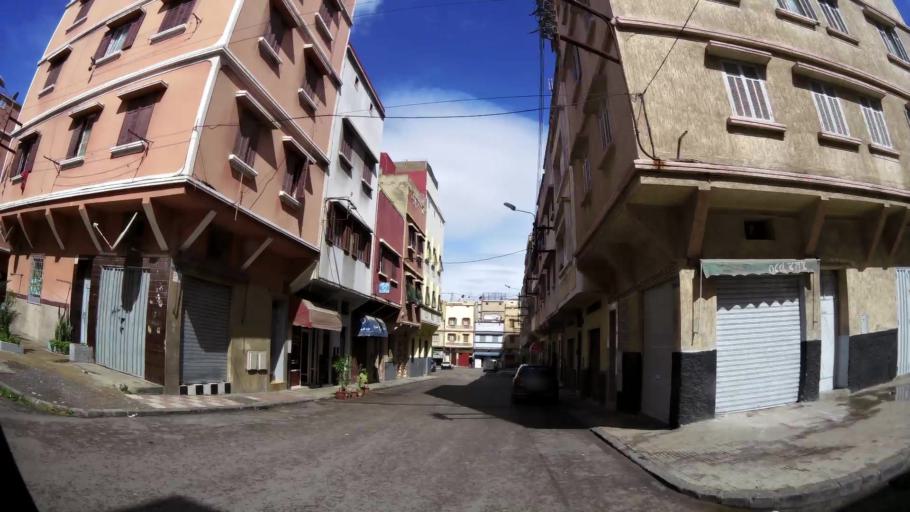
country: MA
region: Grand Casablanca
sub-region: Casablanca
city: Casablanca
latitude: 33.5648
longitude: -7.5928
